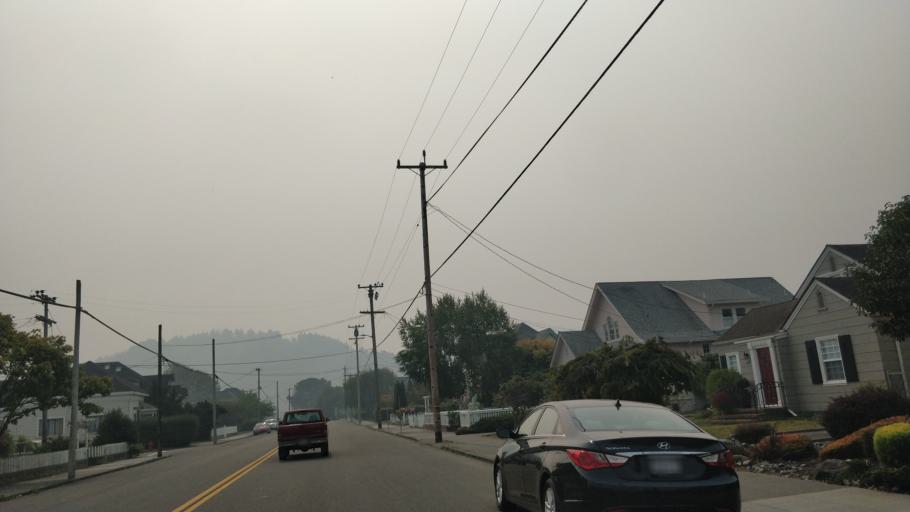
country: US
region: California
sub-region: Humboldt County
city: Ferndale
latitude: 40.5831
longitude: -124.2598
